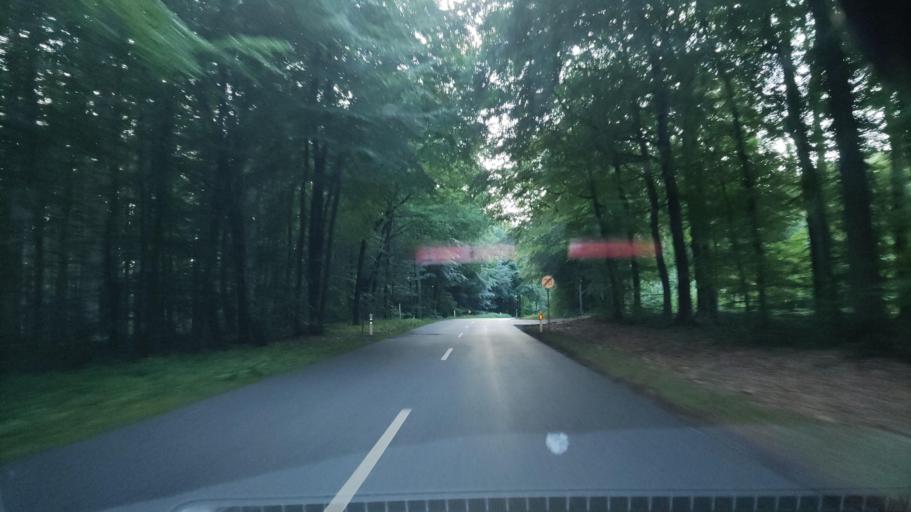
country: DE
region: Lower Saxony
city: Bispingen
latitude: 53.1235
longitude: 10.0520
